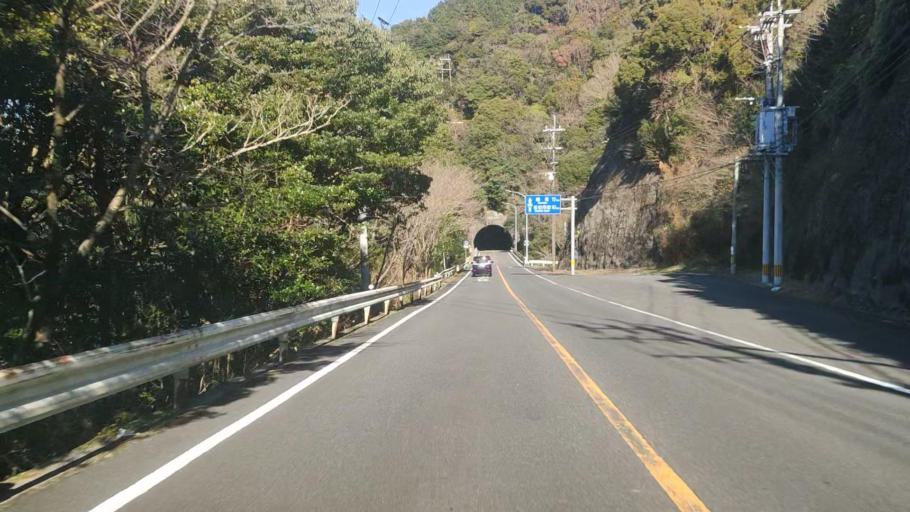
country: JP
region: Oita
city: Saiki
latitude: 32.8907
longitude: 131.9415
